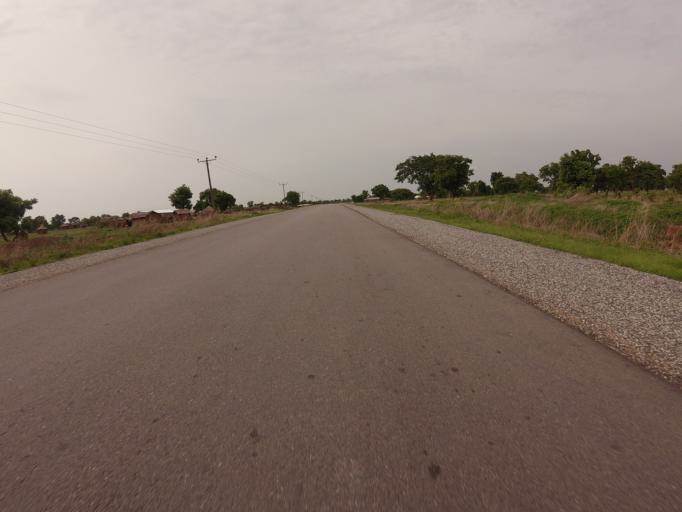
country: GH
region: Northern
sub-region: Yendi
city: Yendi
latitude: 9.8256
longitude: -0.1206
